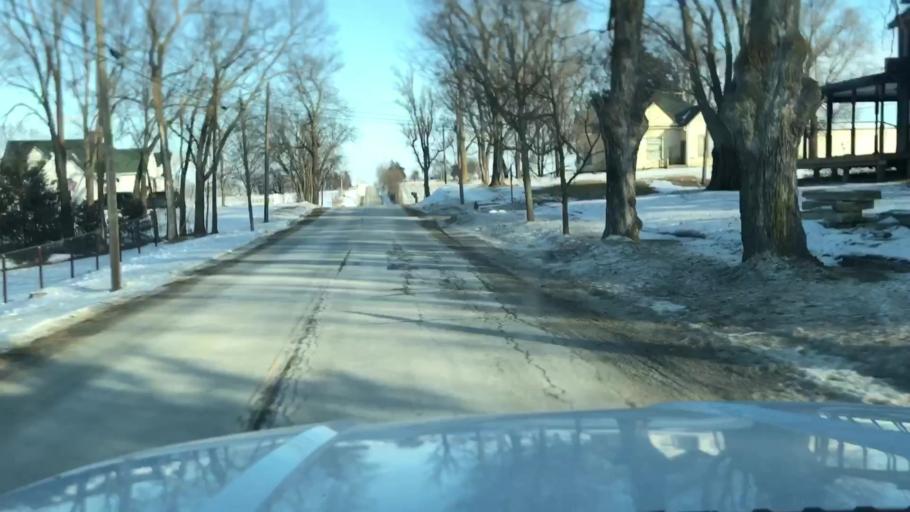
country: US
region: Missouri
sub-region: Andrew County
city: Savannah
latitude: 40.0251
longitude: -94.9698
